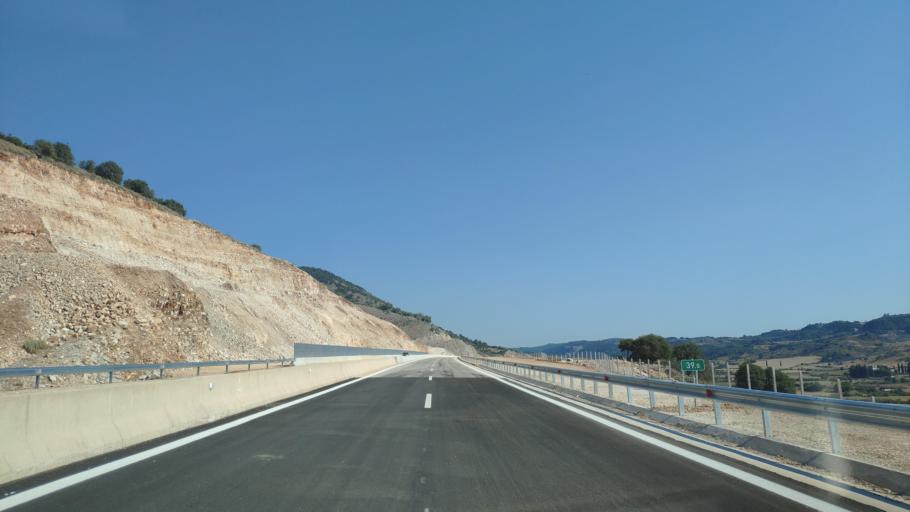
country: GR
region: West Greece
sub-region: Nomos Aitolias kai Akarnanias
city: Katouna
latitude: 38.8253
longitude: 21.1230
